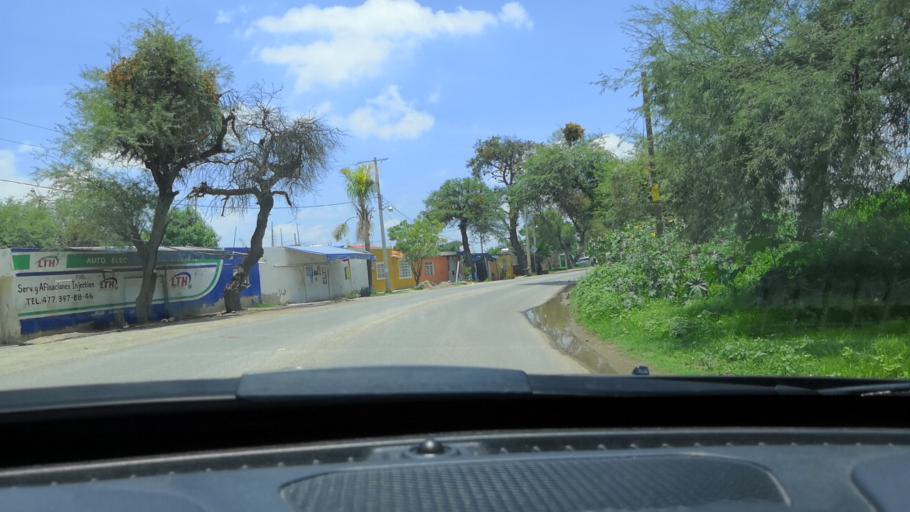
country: MX
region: Guanajuato
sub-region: Leon
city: Ladrilleras del Refugio
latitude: 21.0594
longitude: -101.5575
